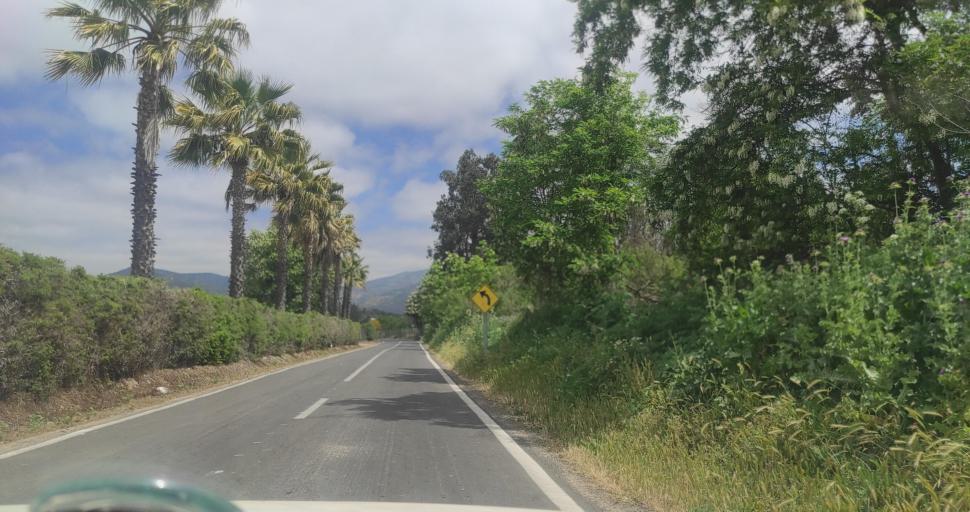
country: CL
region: Valparaiso
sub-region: Provincia de Marga Marga
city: Limache
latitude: -33.0310
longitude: -71.2308
